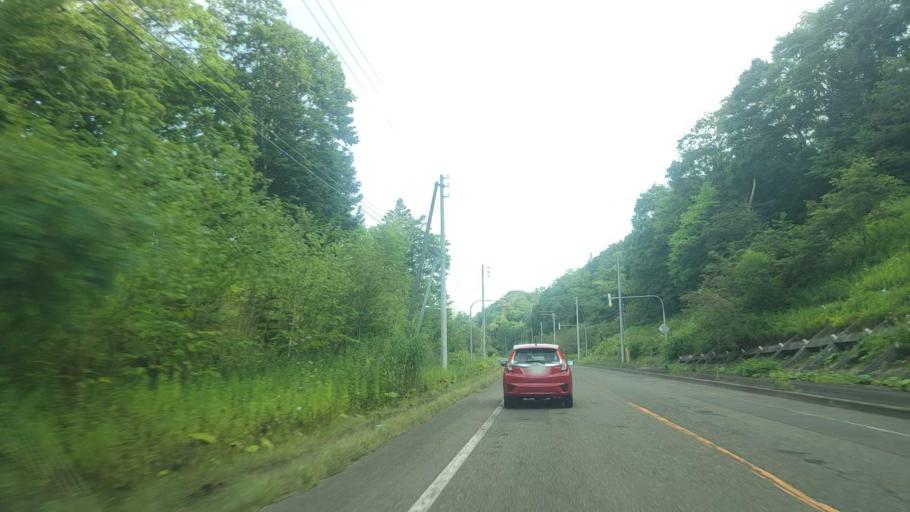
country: JP
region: Hokkaido
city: Iwamizawa
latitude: 43.0253
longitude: 141.9436
